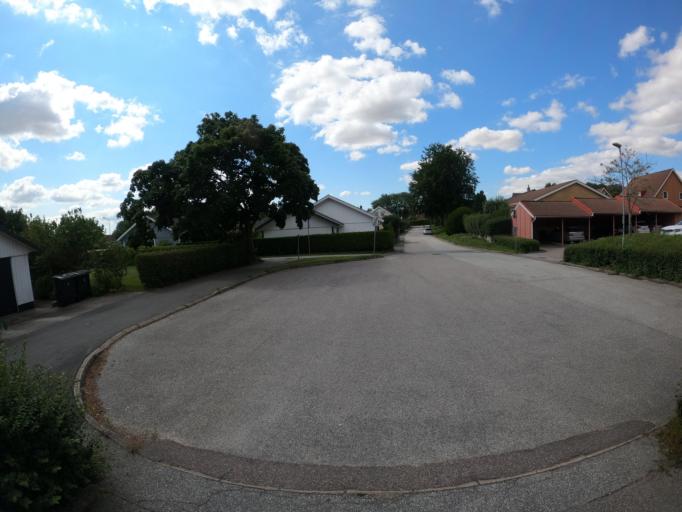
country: SE
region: Skane
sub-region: Lunds Kommun
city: Genarp
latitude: 55.6674
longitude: 13.3649
